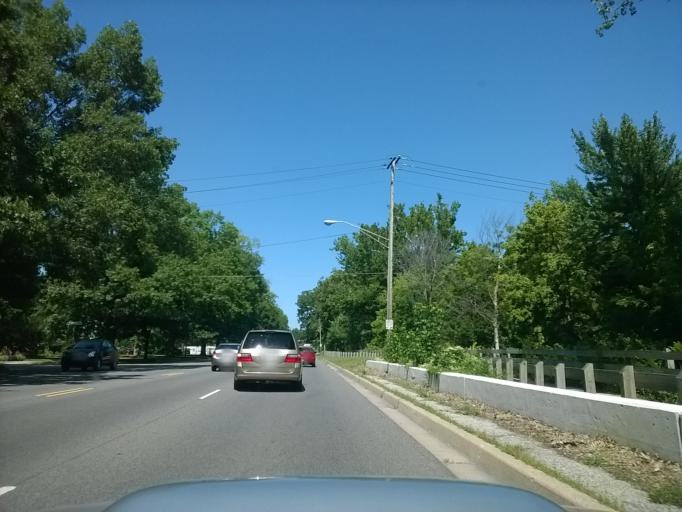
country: US
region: Indiana
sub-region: Marion County
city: Broad Ripple
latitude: 39.8225
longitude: -86.1348
